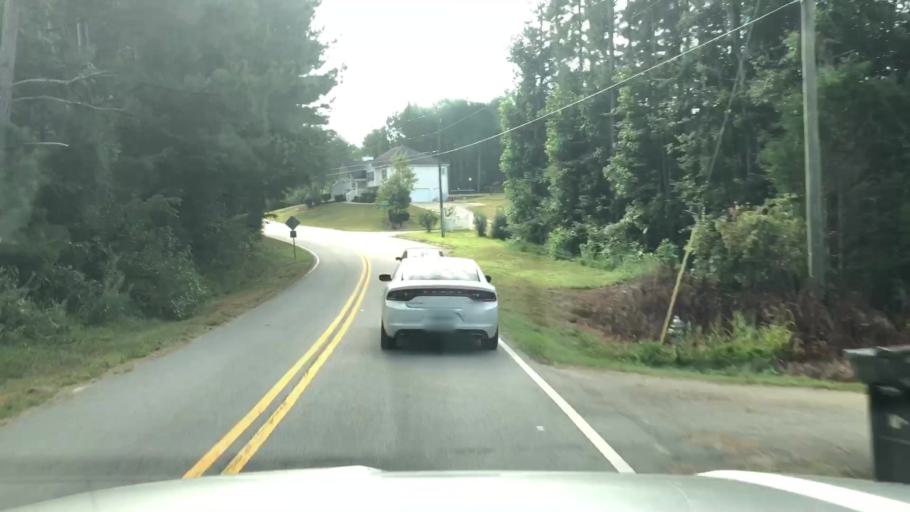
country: US
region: Georgia
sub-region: Paulding County
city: Dallas
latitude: 34.0413
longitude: -84.8499
